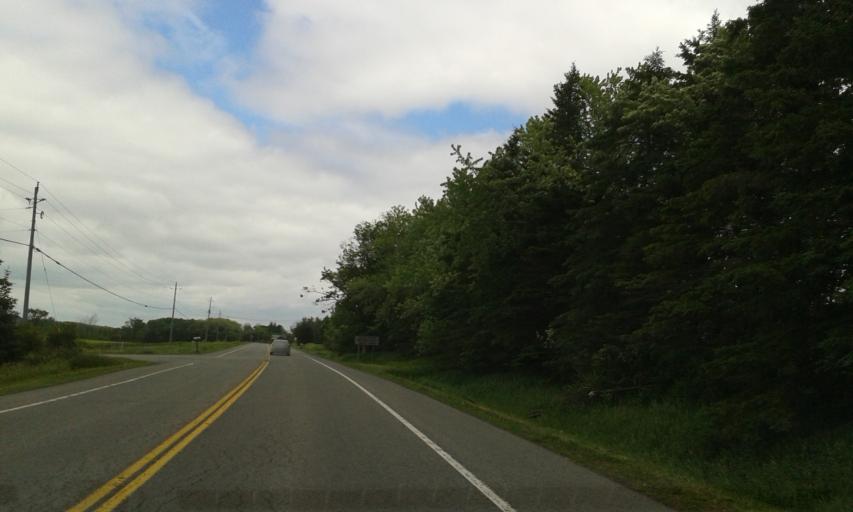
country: CA
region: Ontario
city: Picton
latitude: 44.0601
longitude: -77.0161
